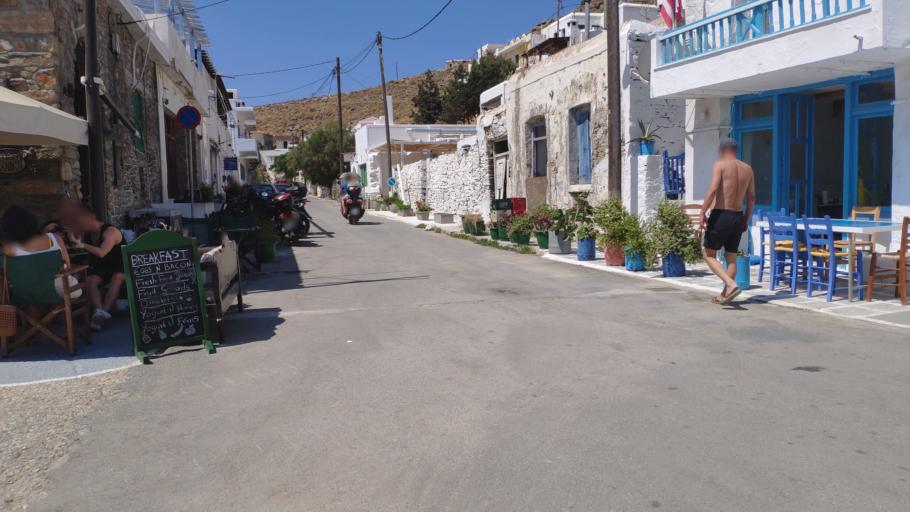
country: GR
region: South Aegean
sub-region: Nomos Kykladon
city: Kythnos
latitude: 37.4421
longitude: 24.4253
